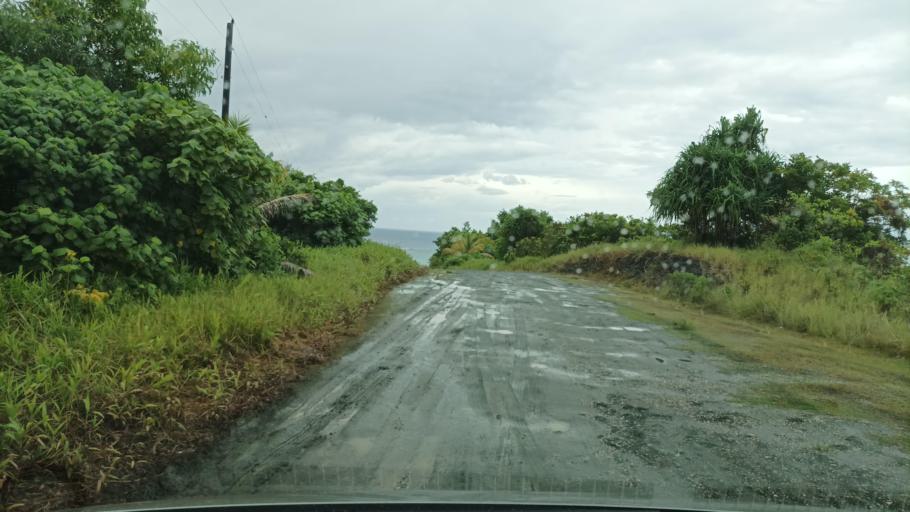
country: FM
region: Yap
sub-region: Rumung Municipality
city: Rumung
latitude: 9.6029
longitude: 138.1762
